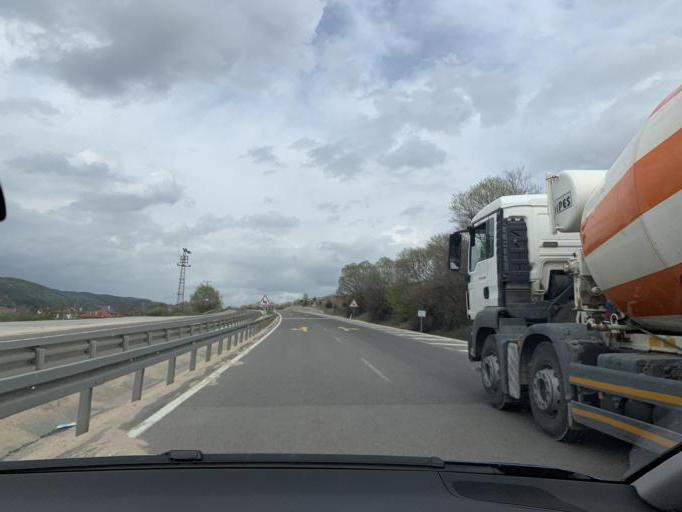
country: TR
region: Bolu
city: Gerede
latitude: 40.7872
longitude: 32.1225
